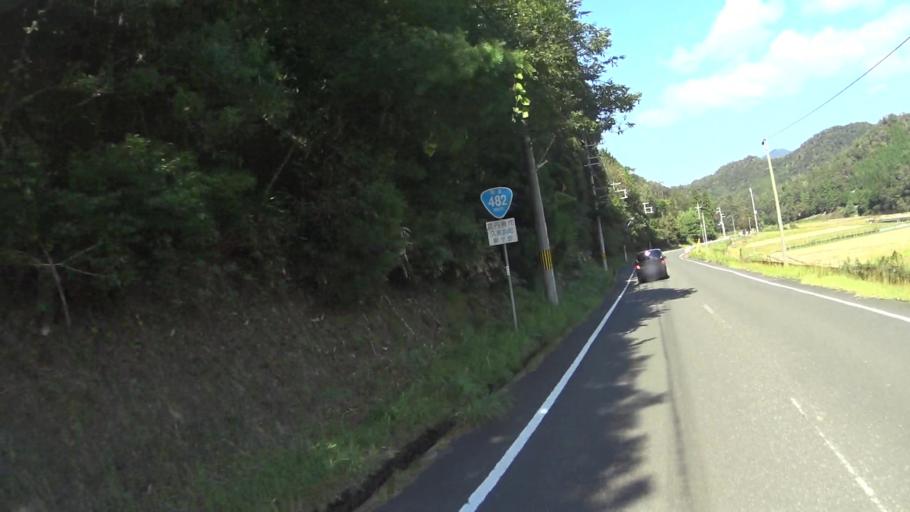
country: JP
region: Hyogo
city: Toyooka
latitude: 35.5546
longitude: 134.9775
